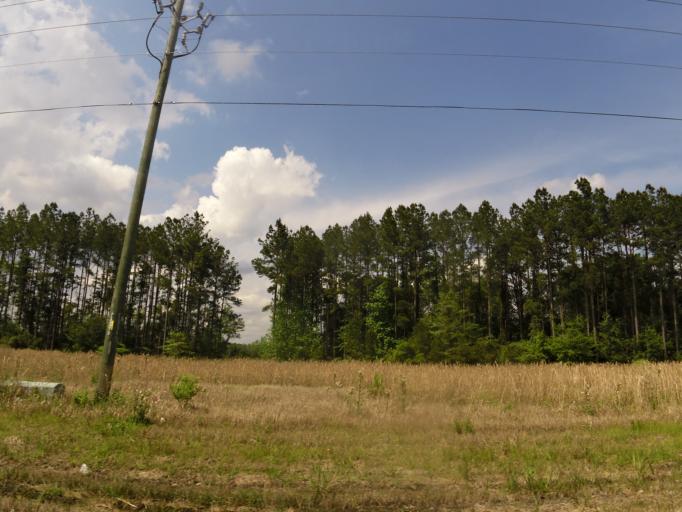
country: US
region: Georgia
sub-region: Camden County
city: Kingsland
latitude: 30.8101
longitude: -81.7825
